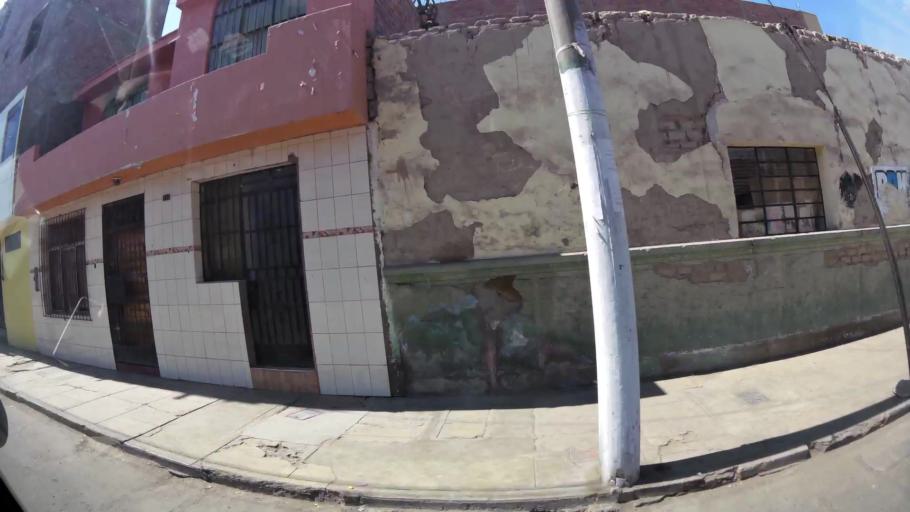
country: PE
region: Ica
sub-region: Provincia de Ica
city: Ica
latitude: -14.0698
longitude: -75.7262
